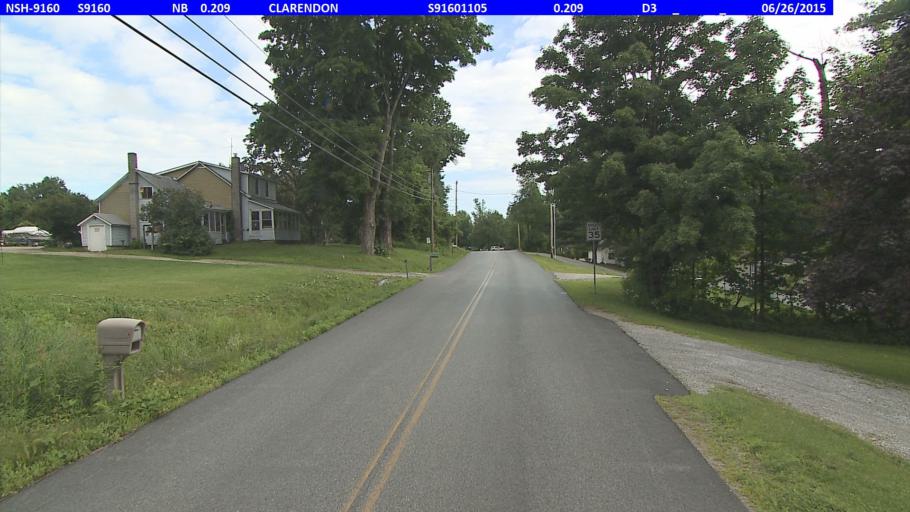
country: US
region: Vermont
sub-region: Rutland County
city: Rutland
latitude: 43.5306
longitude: -72.9450
